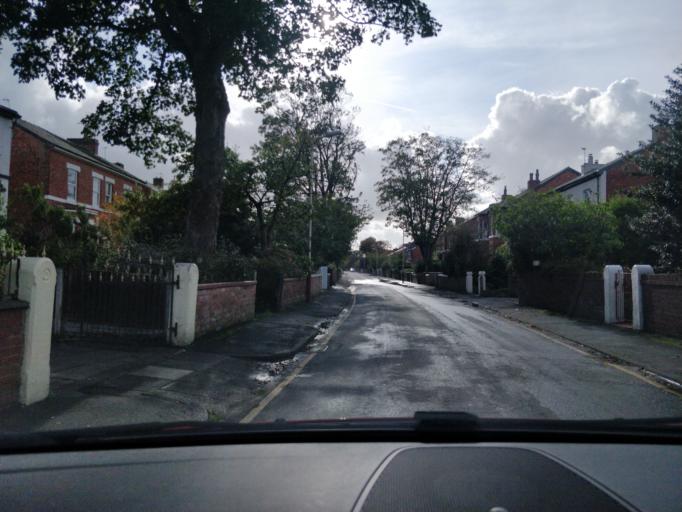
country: GB
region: England
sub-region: Sefton
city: Southport
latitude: 53.6361
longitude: -3.0104
